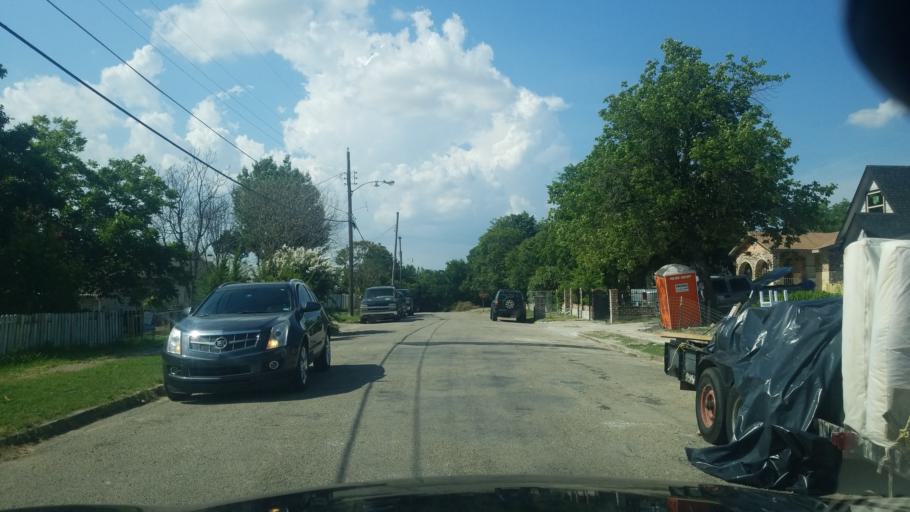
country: US
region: Texas
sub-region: Dallas County
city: Dallas
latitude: 32.7286
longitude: -96.8078
